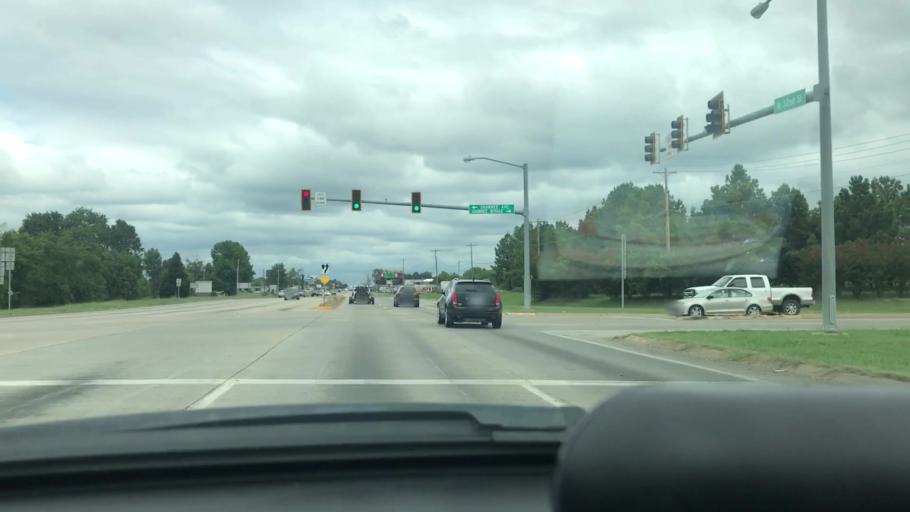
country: US
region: Oklahoma
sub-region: Muskogee County
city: Muskogee
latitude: 35.7693
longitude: -95.4024
